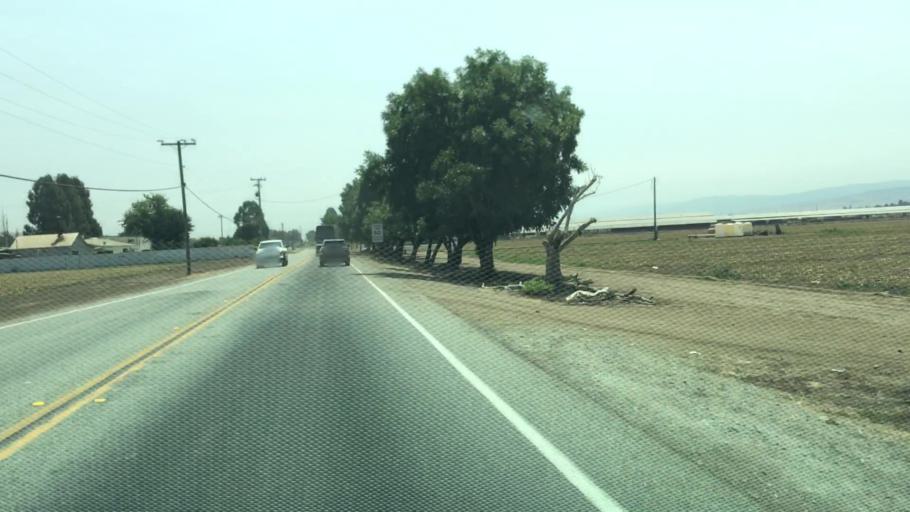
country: US
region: California
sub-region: Santa Clara County
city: Gilroy
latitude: 37.0337
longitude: -121.5327
